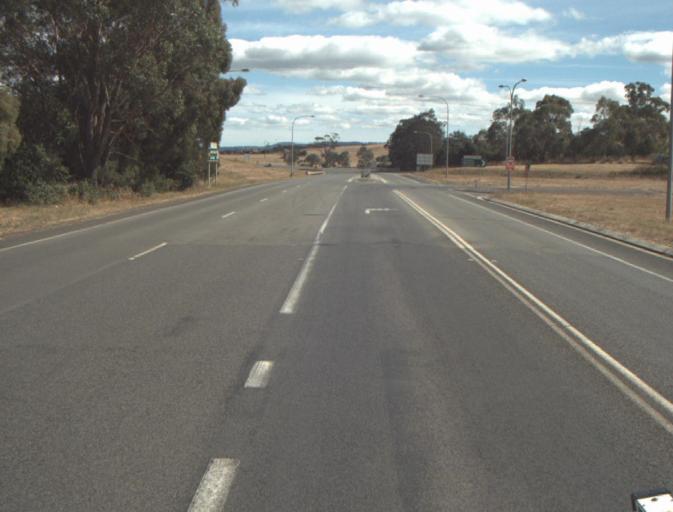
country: AU
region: Tasmania
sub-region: Launceston
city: Newnham
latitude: -41.3992
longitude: 147.1159
